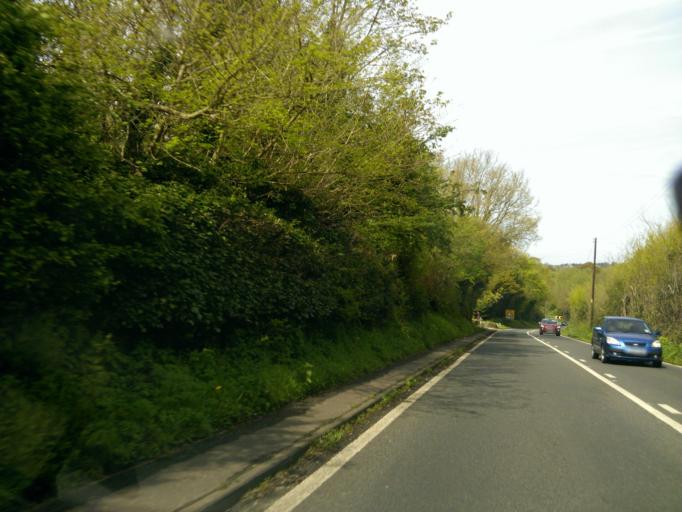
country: GB
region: England
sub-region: Essex
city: Earls Colne
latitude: 51.9292
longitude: 0.6860
